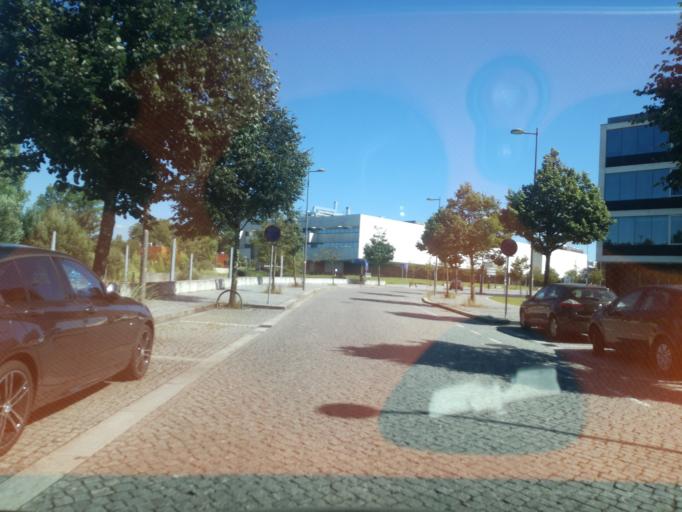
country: PT
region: Porto
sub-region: Matosinhos
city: Sao Mamede de Infesta
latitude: 41.1771
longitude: -8.6044
